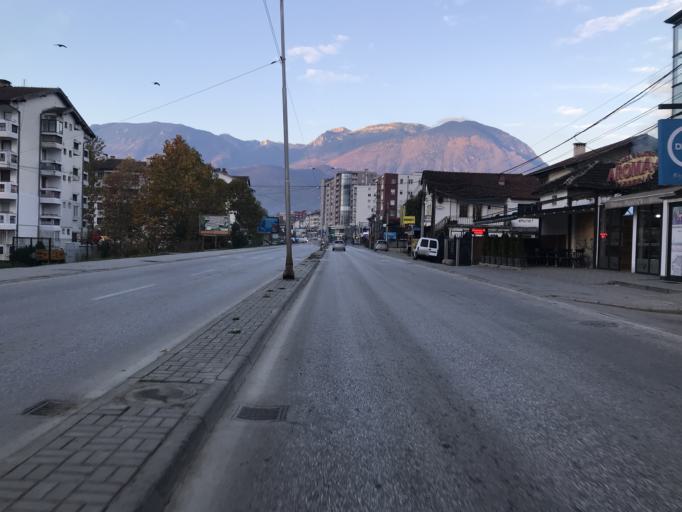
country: XK
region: Pec
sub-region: Komuna e Pejes
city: Peje
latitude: 42.6687
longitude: 20.3057
